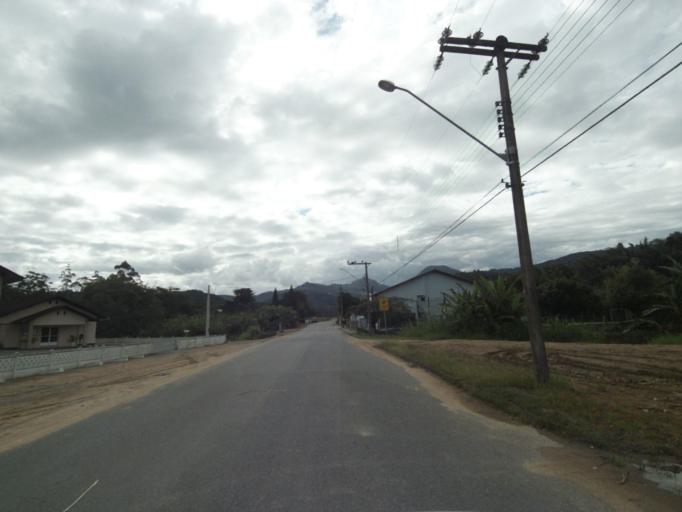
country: BR
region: Santa Catarina
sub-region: Pomerode
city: Pomerode
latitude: -26.7219
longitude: -49.2037
